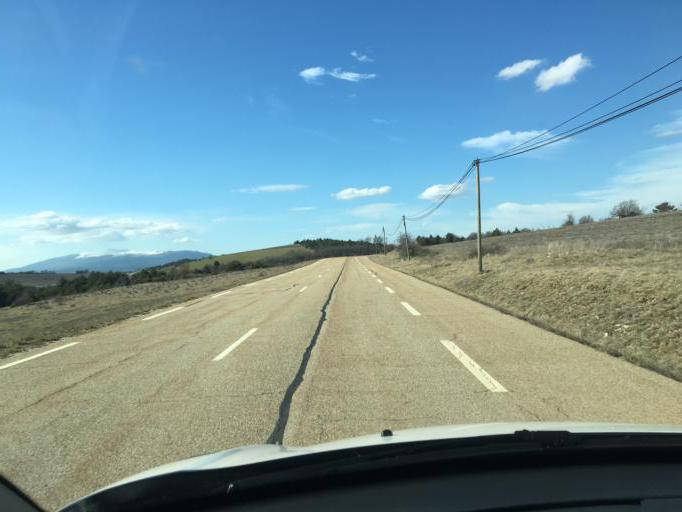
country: FR
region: Provence-Alpes-Cote d'Azur
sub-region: Departement du Vaucluse
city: Sault
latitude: 44.0229
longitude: 5.4689
